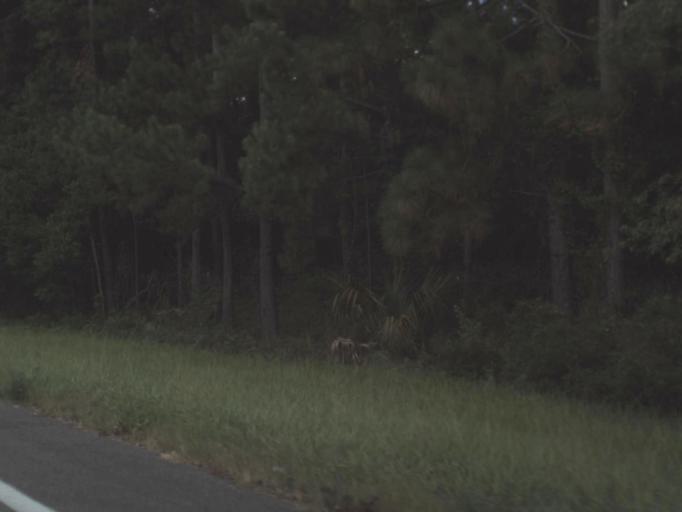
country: US
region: Florida
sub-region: Taylor County
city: Perry
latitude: 30.1014
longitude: -83.6169
